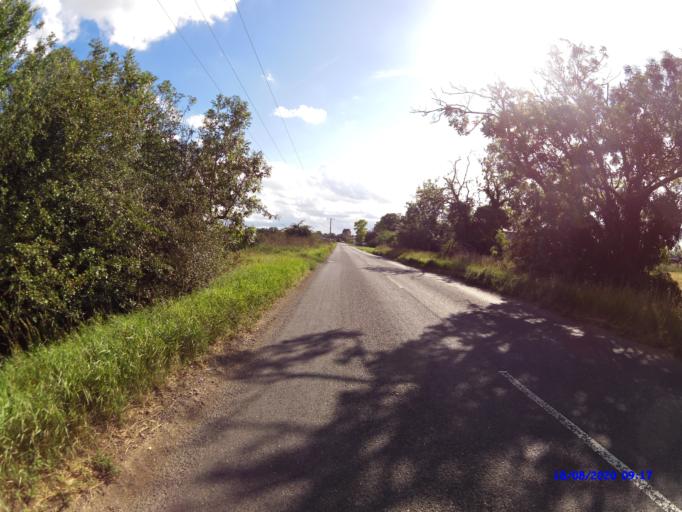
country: GB
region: England
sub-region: Cambridgeshire
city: Ramsey
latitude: 52.4581
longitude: -0.1071
